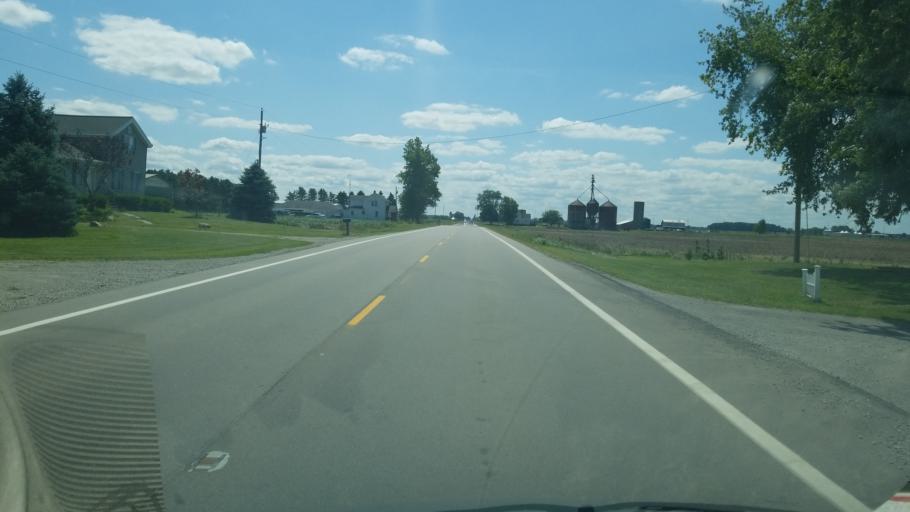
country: US
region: Ohio
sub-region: Fulton County
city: Delta
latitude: 41.7120
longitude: -84.0373
